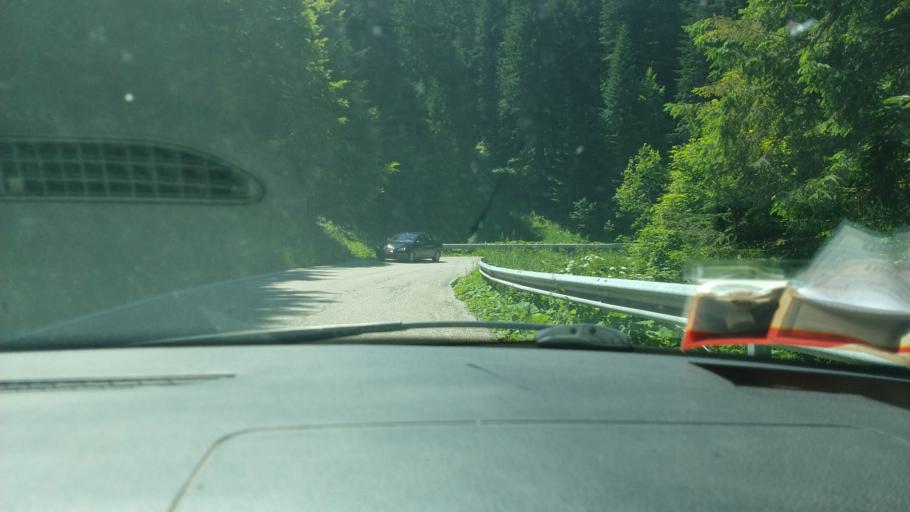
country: IT
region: Veneto
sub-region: Provincia di Vicenza
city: Lastebasse
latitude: 45.9047
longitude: 11.2217
